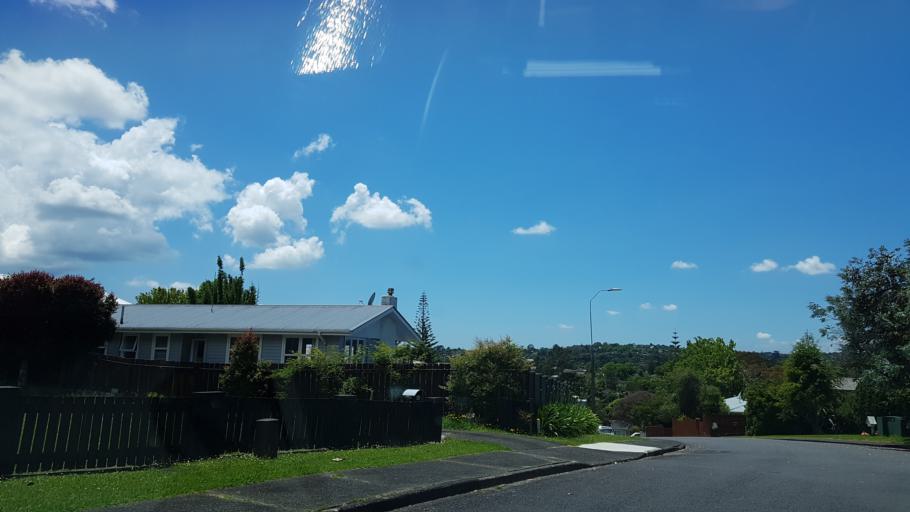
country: NZ
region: Auckland
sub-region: Auckland
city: North Shore
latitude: -36.7957
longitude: 174.6932
